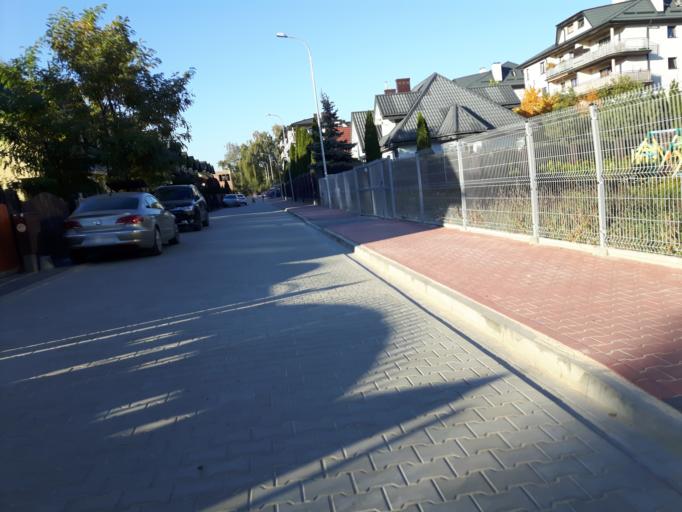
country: PL
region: Masovian Voivodeship
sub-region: Powiat wolominski
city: Zabki
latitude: 52.2806
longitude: 21.1298
